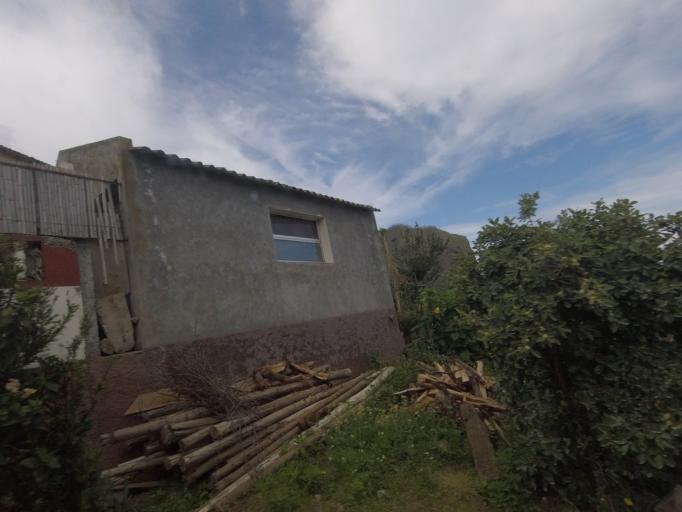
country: PT
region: Madeira
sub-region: Santana
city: Santana
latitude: 32.7661
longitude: -16.8265
